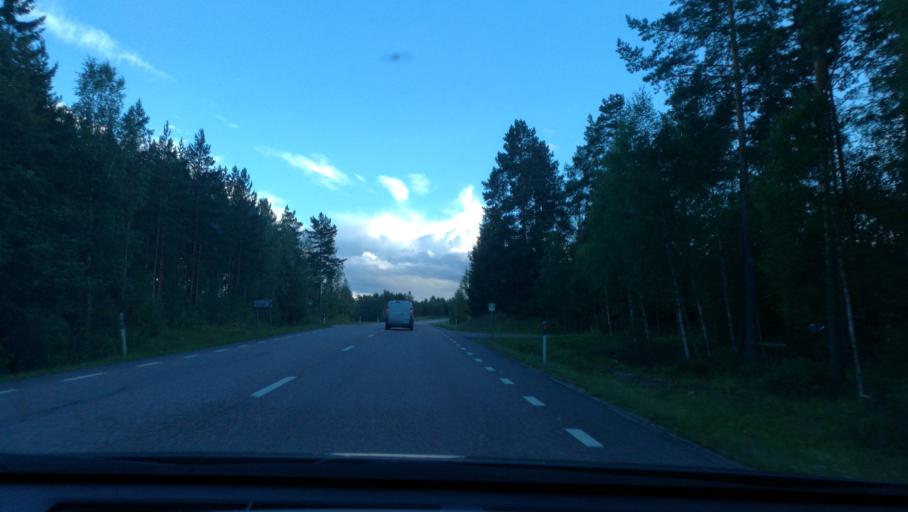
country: SE
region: Soedermanland
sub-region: Katrineholms Kommun
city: Katrineholm
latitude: 59.0464
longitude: 16.2204
